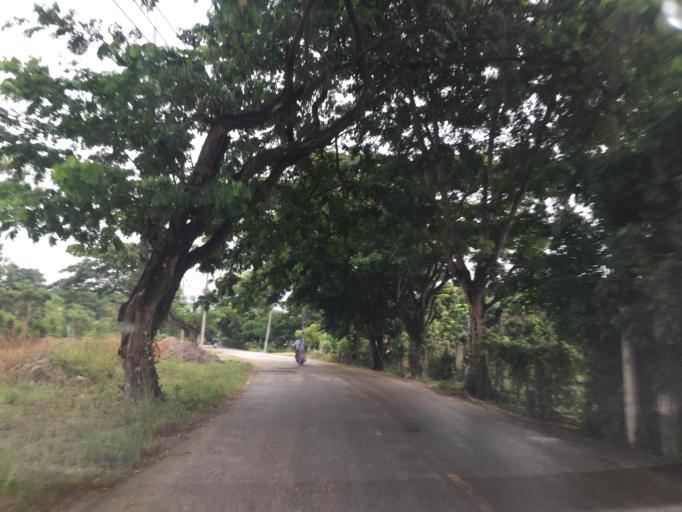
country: TH
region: Lamphun
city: Ban Thi
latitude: 18.6641
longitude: 99.0727
